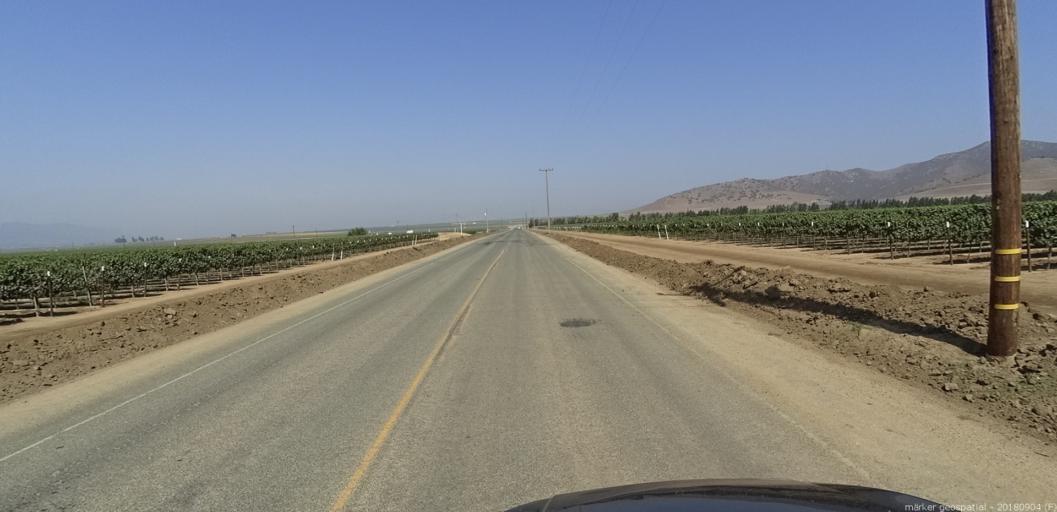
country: US
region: California
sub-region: Monterey County
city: Gonzales
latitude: 36.5520
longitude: -121.4418
